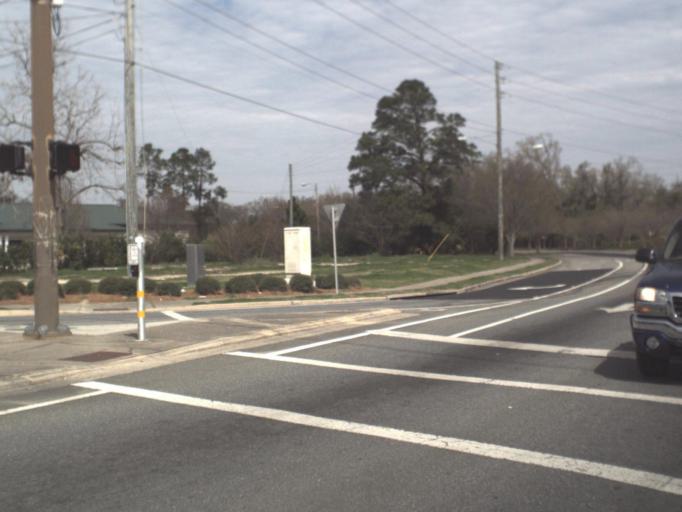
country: US
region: Florida
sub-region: Leon County
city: Tallahassee
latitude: 30.4531
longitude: -84.3379
